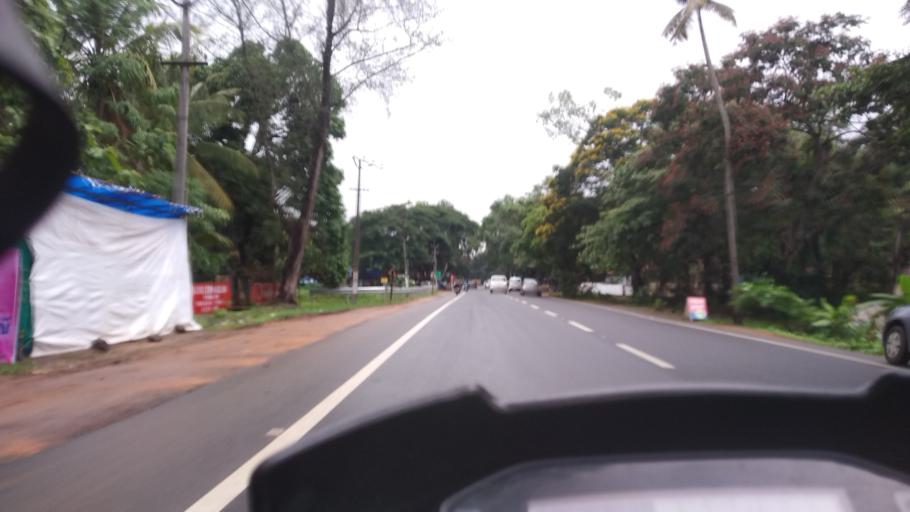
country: IN
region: Kerala
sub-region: Alappuzha
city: Mavelikara
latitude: 9.3055
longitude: 76.4322
